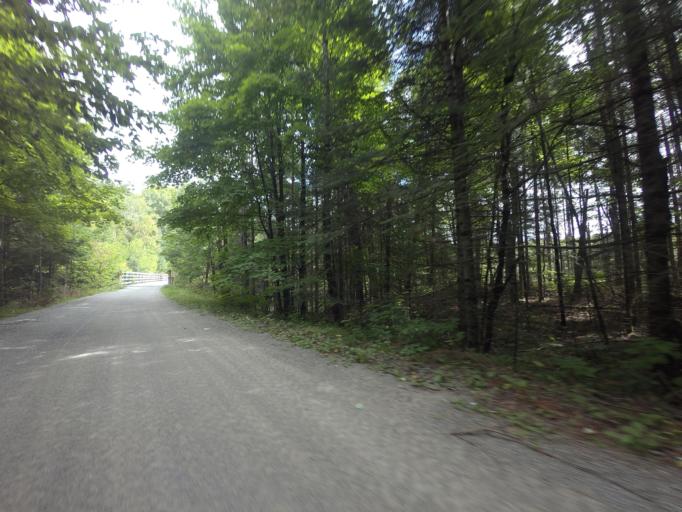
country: CA
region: Ontario
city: Omemee
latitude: 44.7602
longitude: -78.6743
